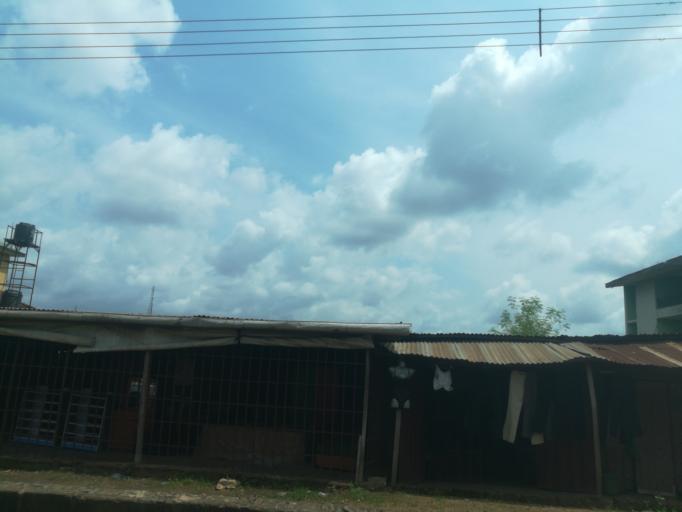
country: NG
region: Oyo
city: Ibadan
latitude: 7.3560
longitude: 3.8784
